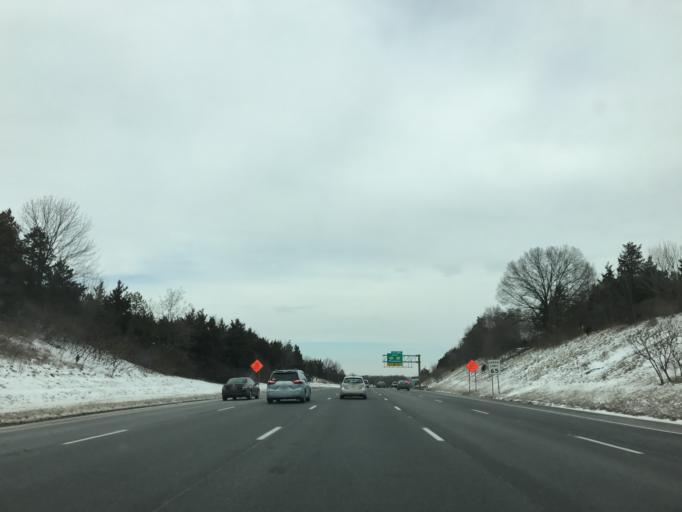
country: US
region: New Jersey
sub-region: Somerset County
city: Bedminster
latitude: 40.6481
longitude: -74.6459
